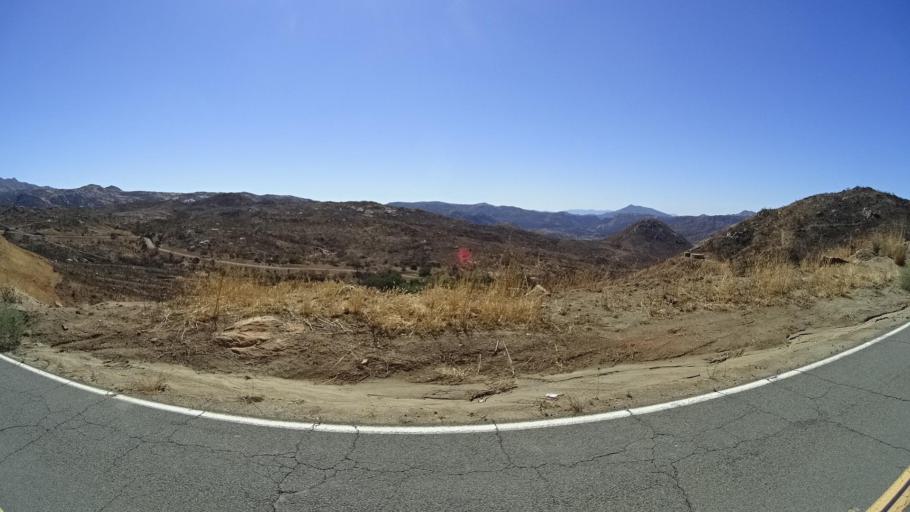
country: US
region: California
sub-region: San Diego County
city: Descanso
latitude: 32.7466
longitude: -116.6751
